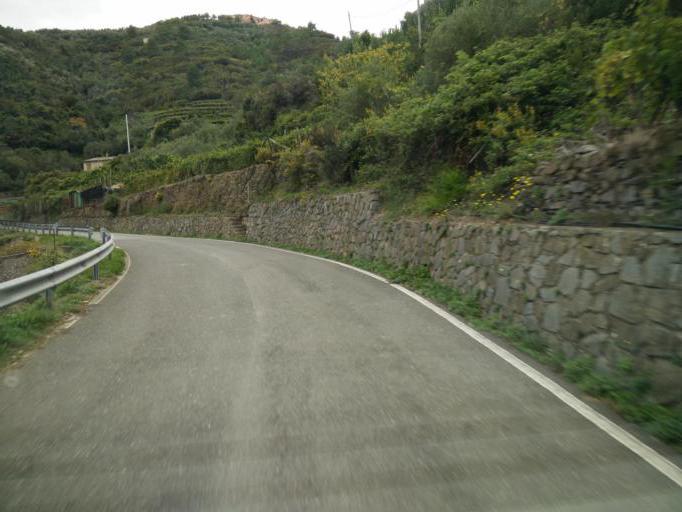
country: IT
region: Liguria
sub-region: Provincia di La Spezia
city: Riomaggiore
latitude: 44.1113
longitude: 9.7345
